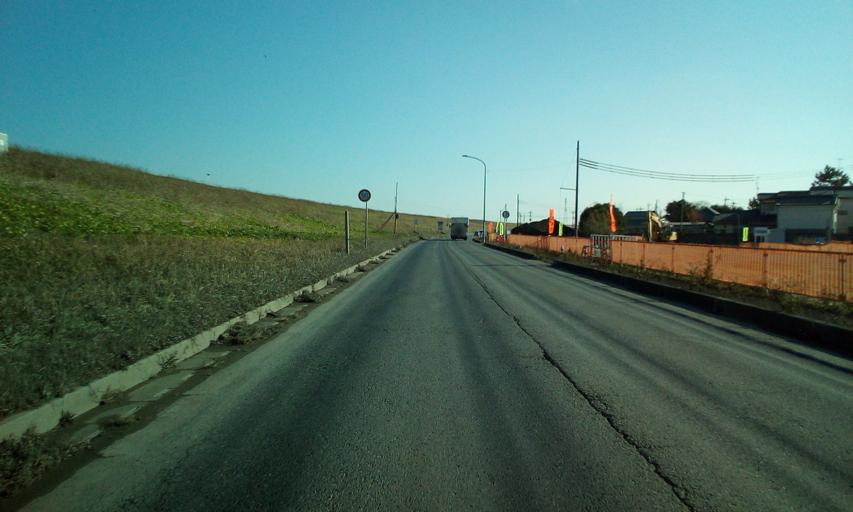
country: JP
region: Chiba
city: Noda
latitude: 35.9274
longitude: 139.8607
